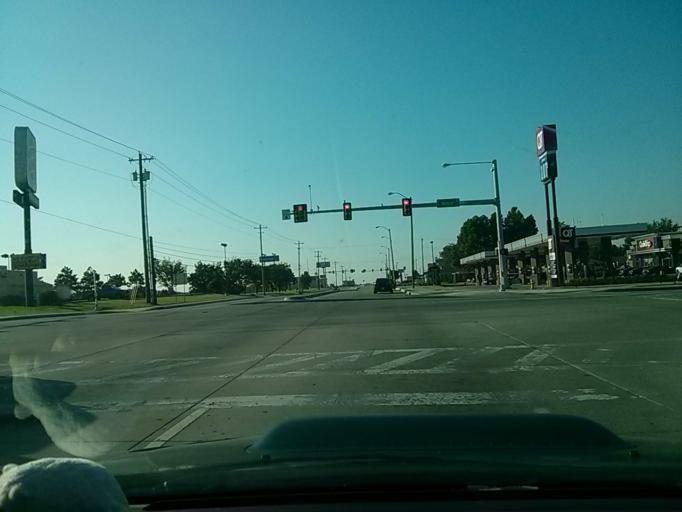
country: US
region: Oklahoma
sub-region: Tulsa County
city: Tulsa
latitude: 36.1610
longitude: -95.8868
